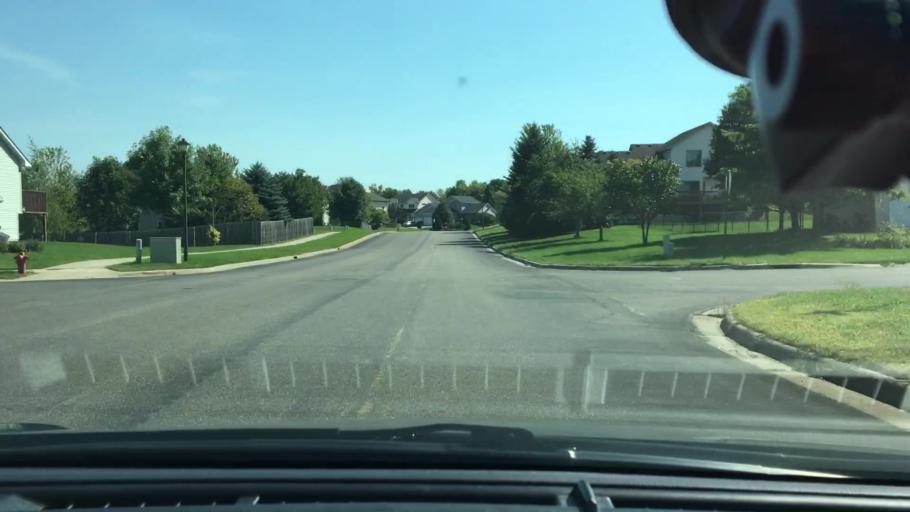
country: US
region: Minnesota
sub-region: Wright County
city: Saint Michael
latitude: 45.2022
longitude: -93.6806
